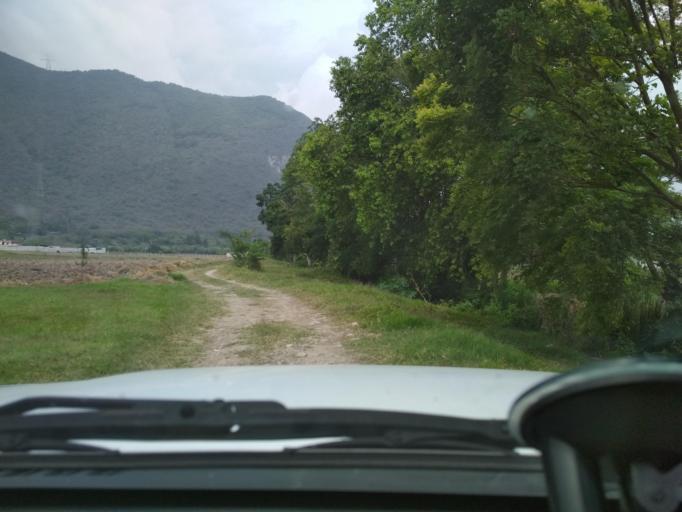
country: MX
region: Veracruz
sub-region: Nogales
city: Taza de Agua Ojo Zarco
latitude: 18.7867
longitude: -97.2054
